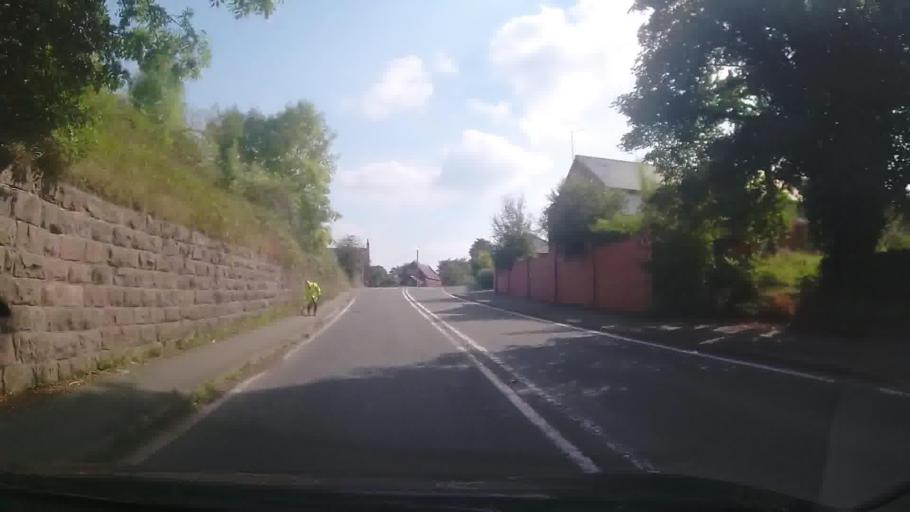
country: GB
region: England
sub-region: Cheshire West and Chester
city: Tiverton
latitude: 53.1337
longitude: -2.6700
